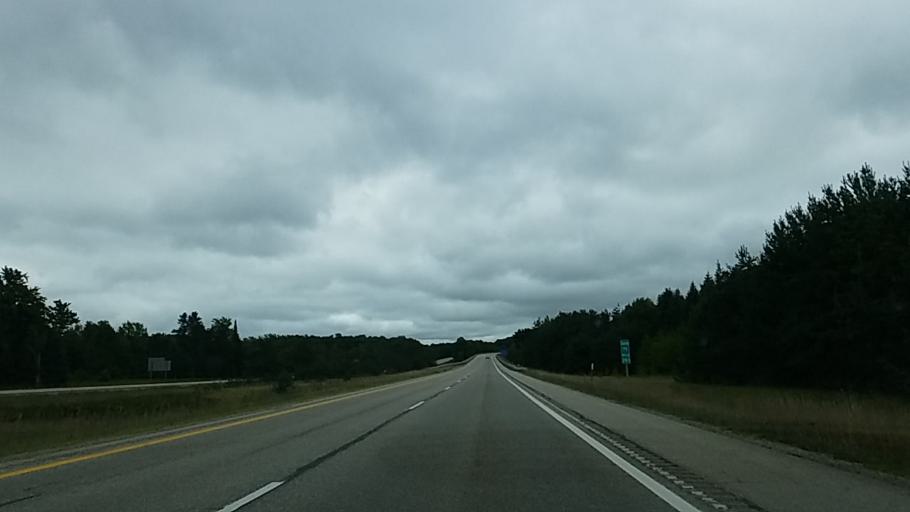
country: US
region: Michigan
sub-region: Otsego County
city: Gaylord
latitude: 45.1307
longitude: -84.6718
